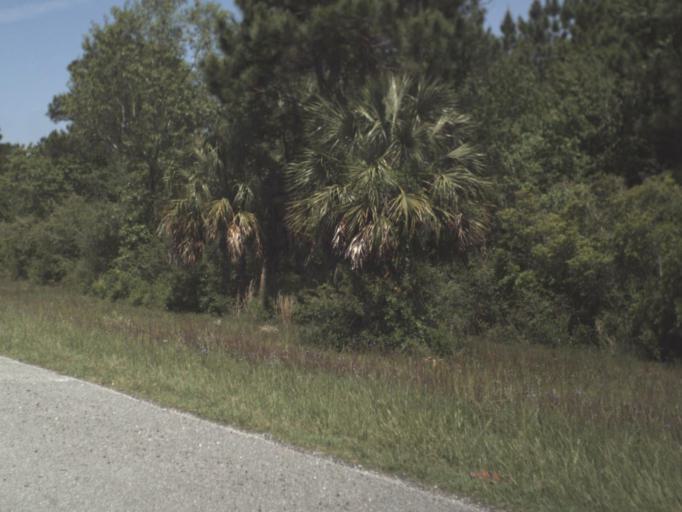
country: US
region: Florida
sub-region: Santa Rosa County
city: Pace
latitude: 30.5342
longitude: -87.1017
